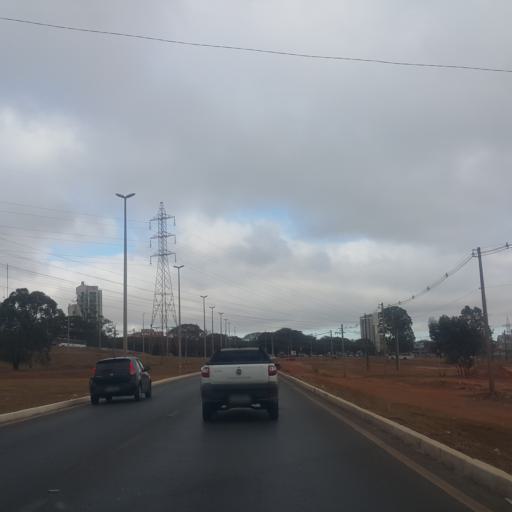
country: BR
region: Federal District
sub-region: Brasilia
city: Brasilia
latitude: -15.8308
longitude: -48.0475
